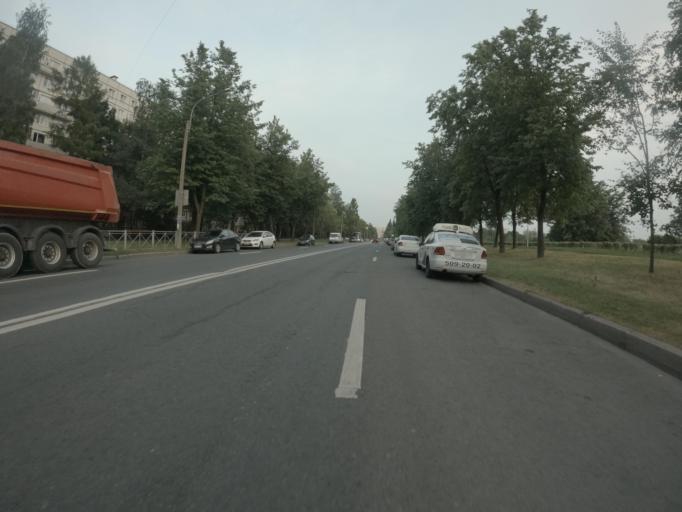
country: RU
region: St.-Petersburg
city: Krasnogvargeisky
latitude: 59.9656
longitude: 30.4311
